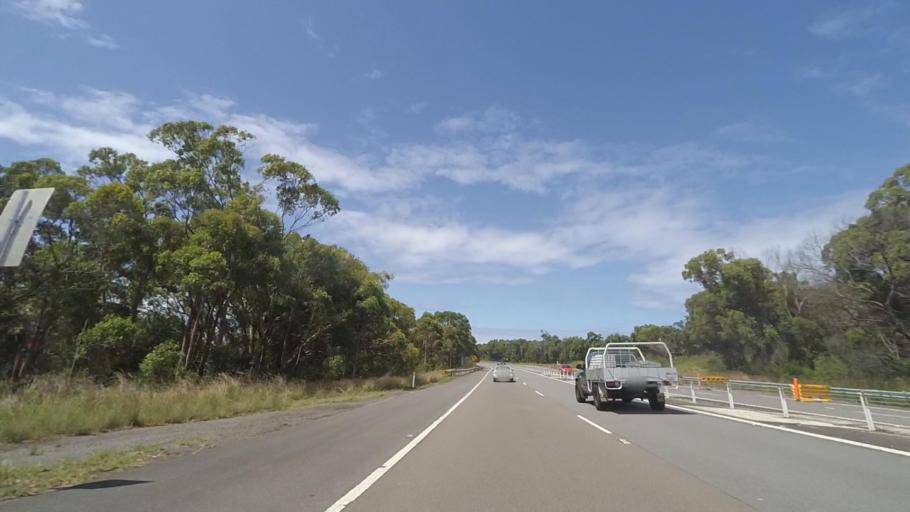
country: AU
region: New South Wales
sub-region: Wyong Shire
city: Kingfisher Shores
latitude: -33.1550
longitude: 151.6111
